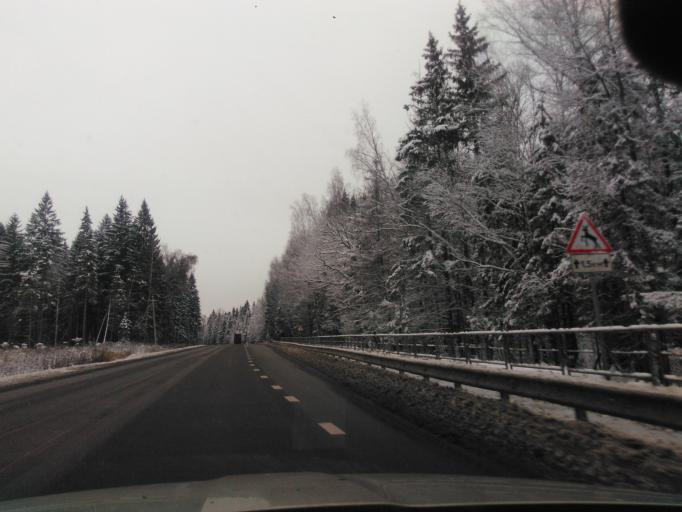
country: RU
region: Moskovskaya
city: Povarovo
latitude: 55.9980
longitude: 37.0368
